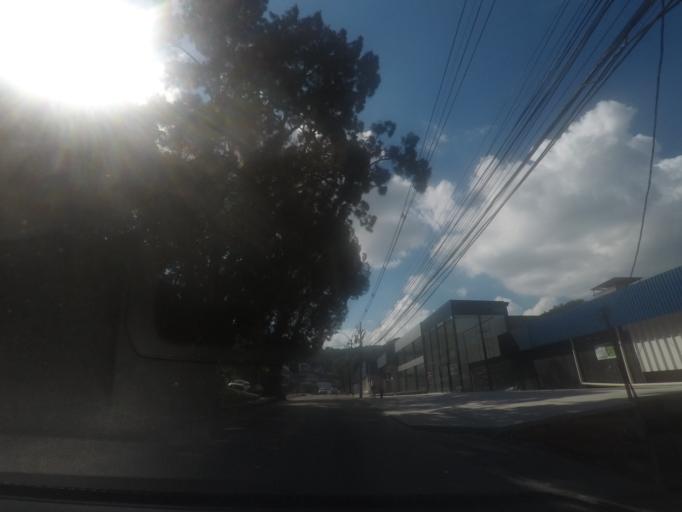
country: BR
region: Rio de Janeiro
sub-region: Petropolis
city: Petropolis
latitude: -22.5332
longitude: -43.2096
